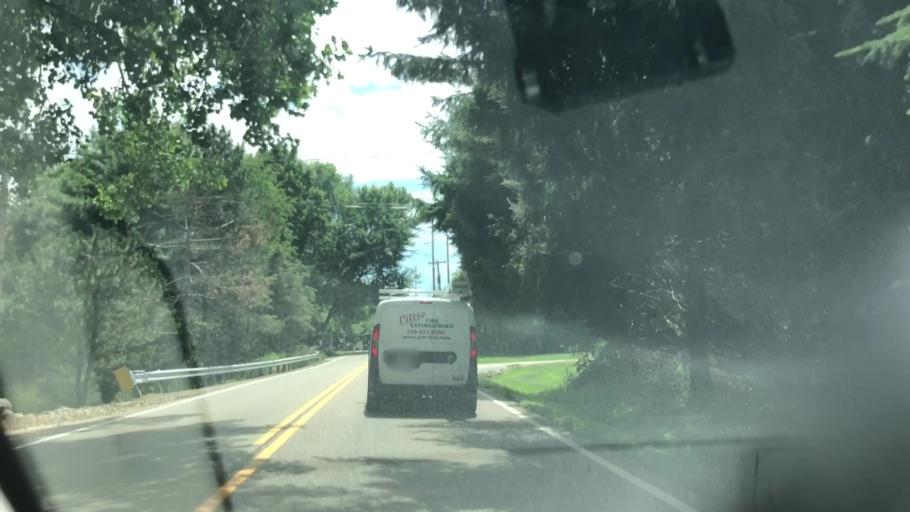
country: US
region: Ohio
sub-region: Summit County
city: Green
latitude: 40.9278
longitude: -81.4961
